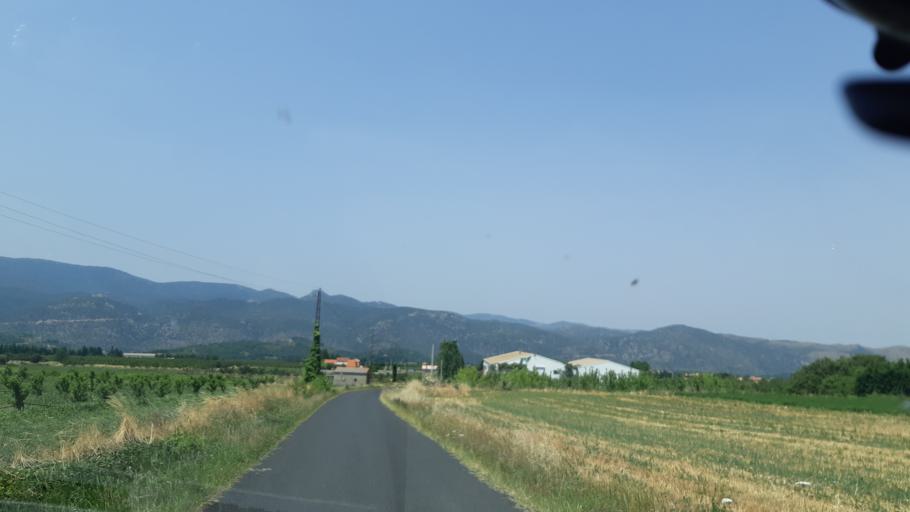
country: FR
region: Languedoc-Roussillon
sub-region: Departement des Pyrenees-Orientales
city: Vinca
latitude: 42.6180
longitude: 2.5189
